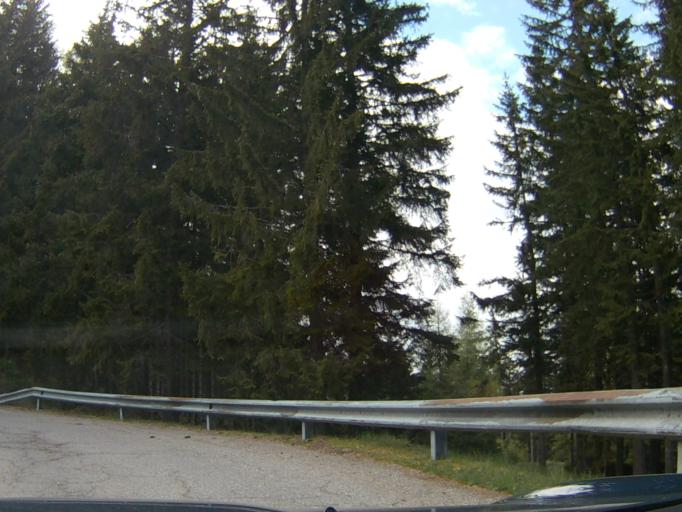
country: AT
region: Carinthia
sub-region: Politischer Bezirk Villach Land
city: Stockenboi
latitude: 46.7433
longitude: 13.5321
